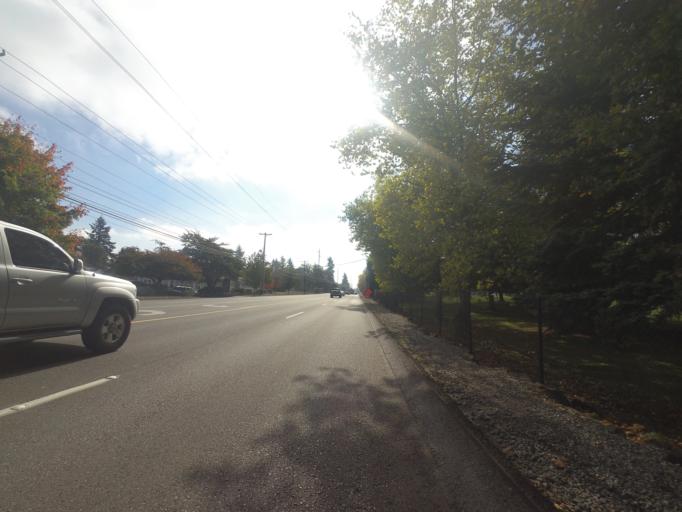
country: US
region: Washington
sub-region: Pierce County
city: Lakewood
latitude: 47.1951
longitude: -122.5088
